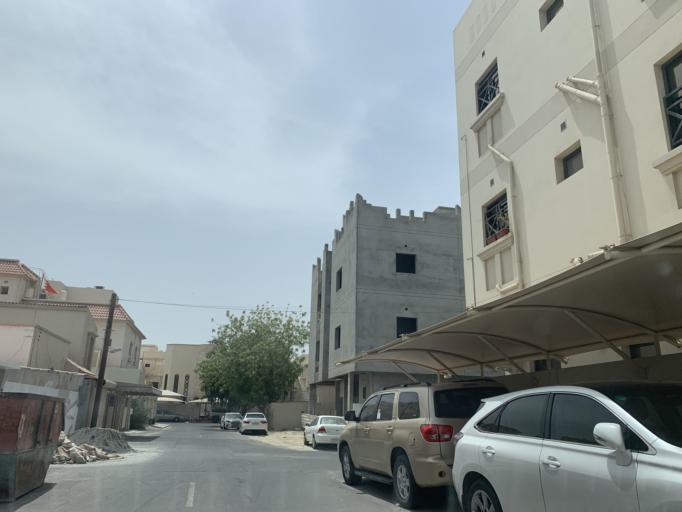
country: BH
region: Northern
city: Ar Rifa'
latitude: 26.1376
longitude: 50.5624
